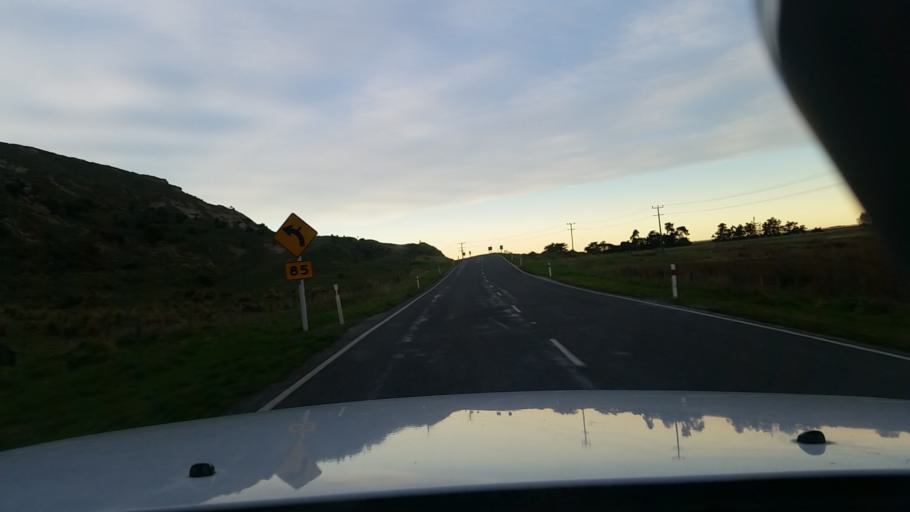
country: NZ
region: Canterbury
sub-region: Selwyn District
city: Lincoln
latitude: -43.7476
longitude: 172.6126
